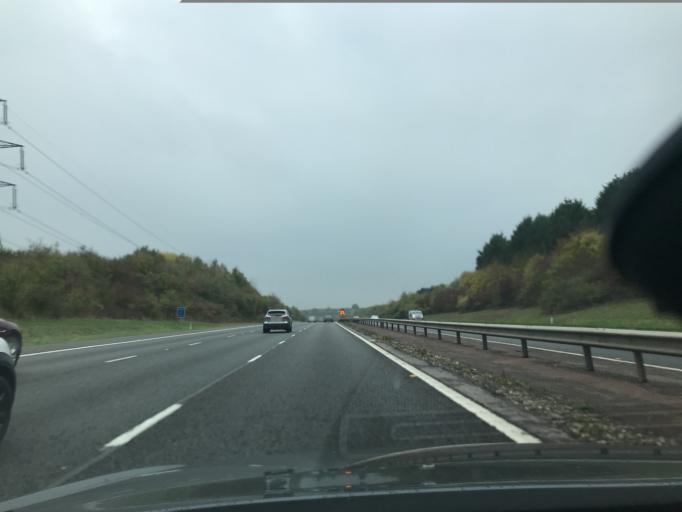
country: GB
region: England
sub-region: Oxfordshire
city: Wheatley
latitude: 51.8193
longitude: -1.1060
